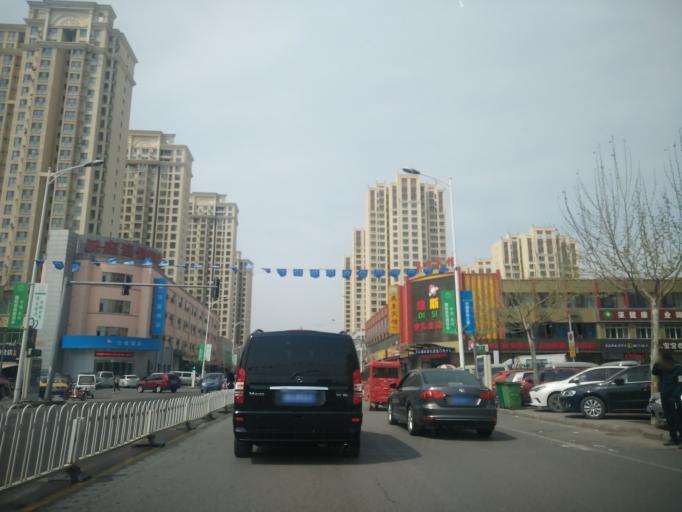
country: CN
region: Beijing
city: Xiji
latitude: 39.7588
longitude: 117.0165
